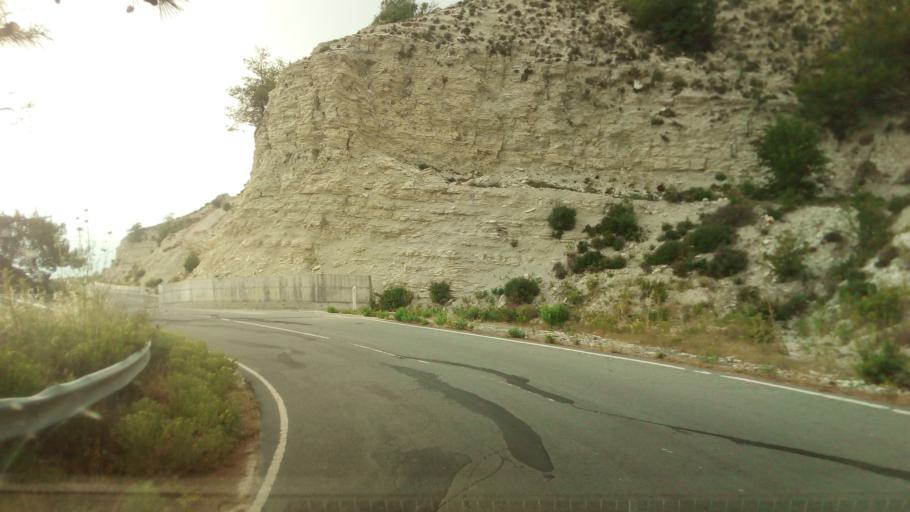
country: CY
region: Limassol
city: Pachna
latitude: 34.8345
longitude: 32.6819
